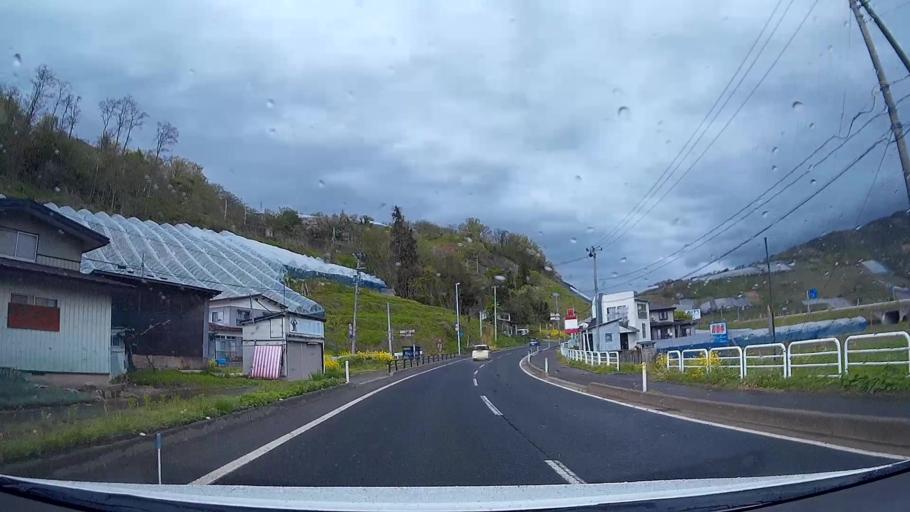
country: JP
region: Yamagata
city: Takahata
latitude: 38.0572
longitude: 140.1726
